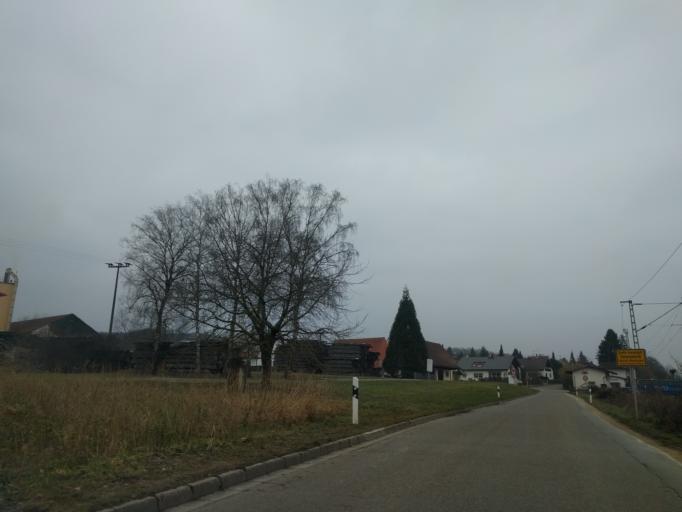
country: DE
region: Bavaria
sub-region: Swabia
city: Harburg
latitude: 48.7307
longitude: 10.7146
